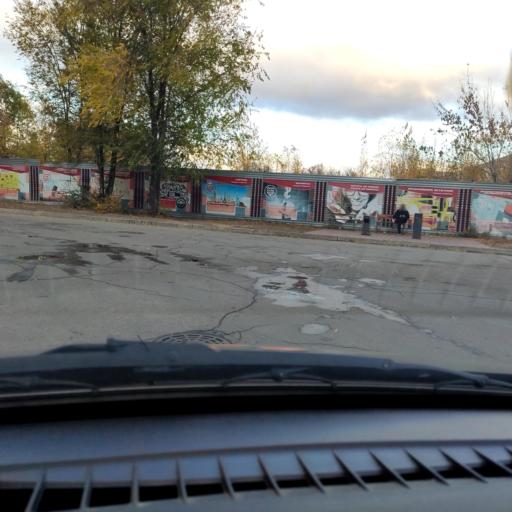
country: RU
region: Samara
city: Tol'yatti
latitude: 53.5171
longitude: 49.2808
